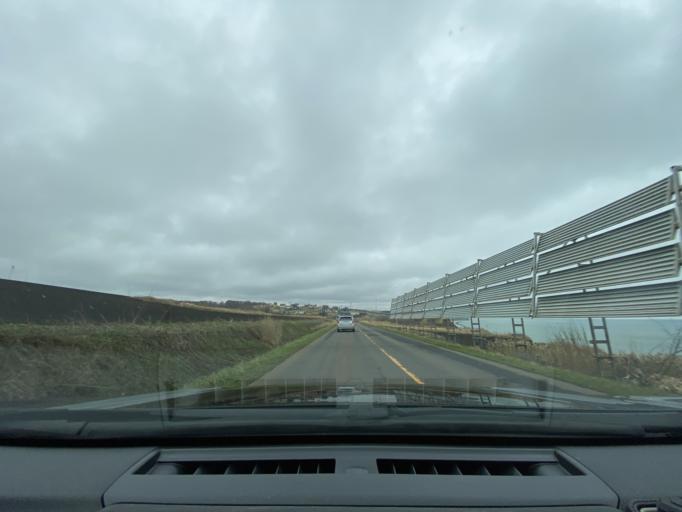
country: JP
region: Hokkaido
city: Ishikari
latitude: 43.3304
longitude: 141.4257
